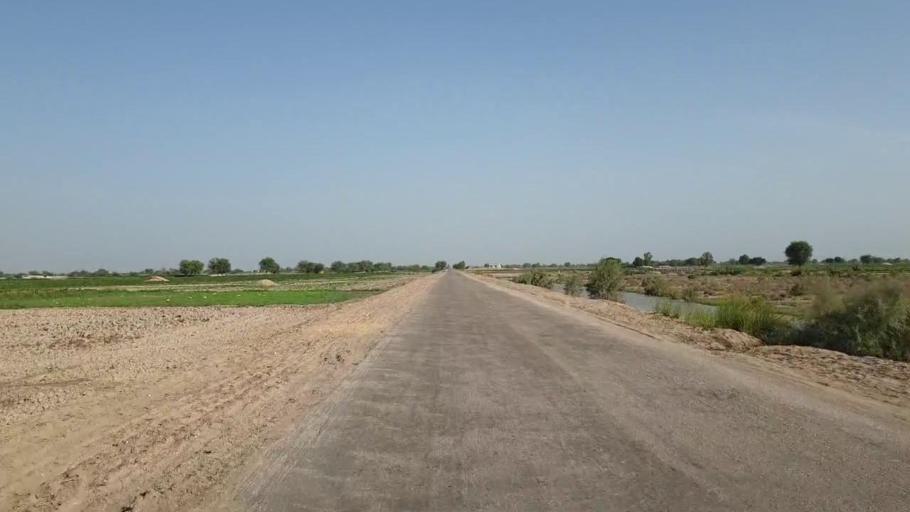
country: PK
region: Sindh
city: Nawabshah
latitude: 26.1468
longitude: 68.4495
